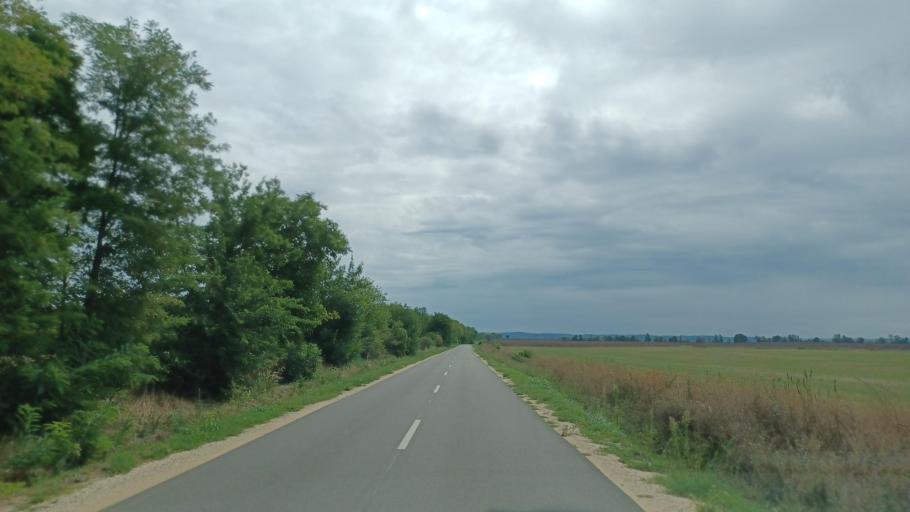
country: HU
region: Tolna
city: Zomba
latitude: 46.4236
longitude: 18.6090
